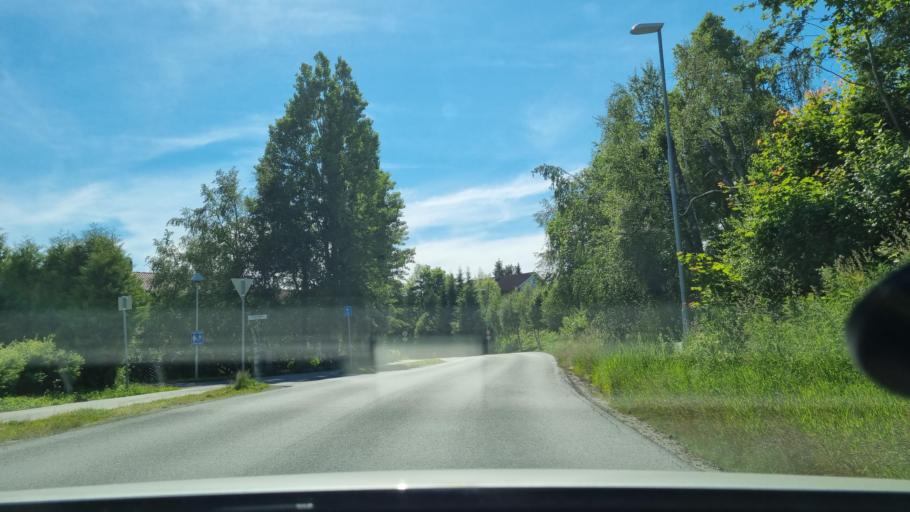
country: NO
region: Sor-Trondelag
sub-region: Trondheim
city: Trondheim
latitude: 63.3852
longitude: 10.3286
